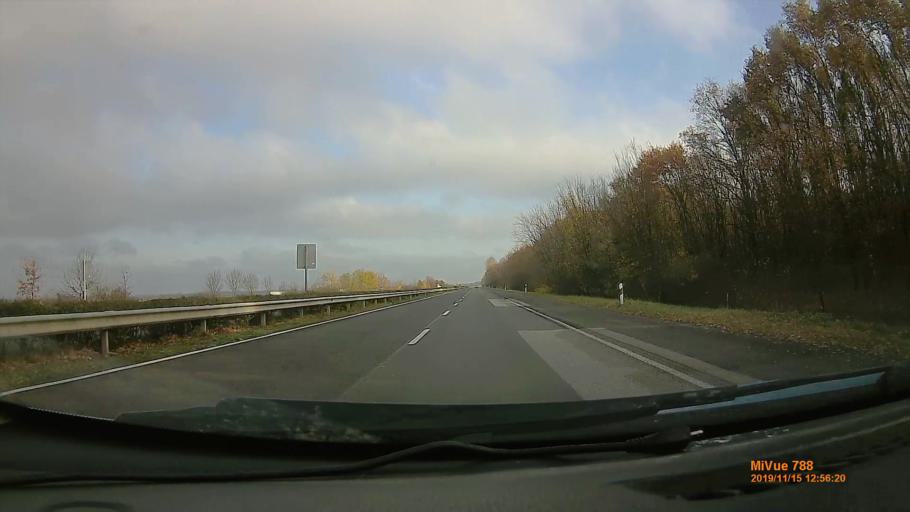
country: HU
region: Bekes
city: Bekescsaba
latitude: 46.6749
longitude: 21.1413
